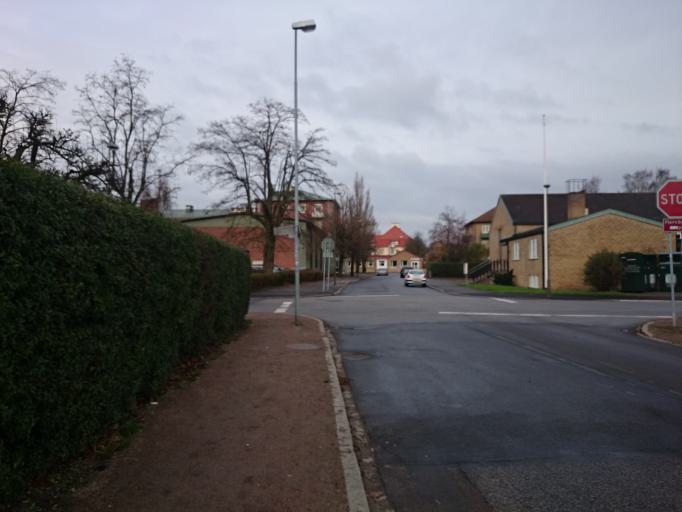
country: SE
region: Skane
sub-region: Malmo
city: Bunkeflostrand
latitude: 55.5800
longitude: 12.9373
